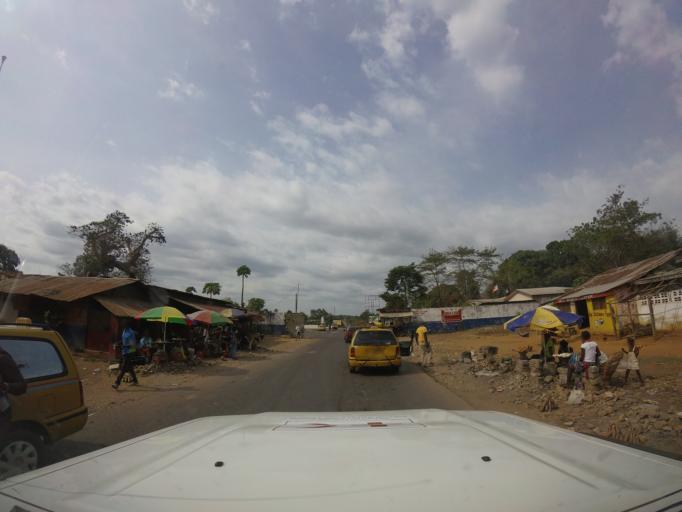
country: LR
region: Bomi
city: Tubmanburg
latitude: 6.6861
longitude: -10.8756
